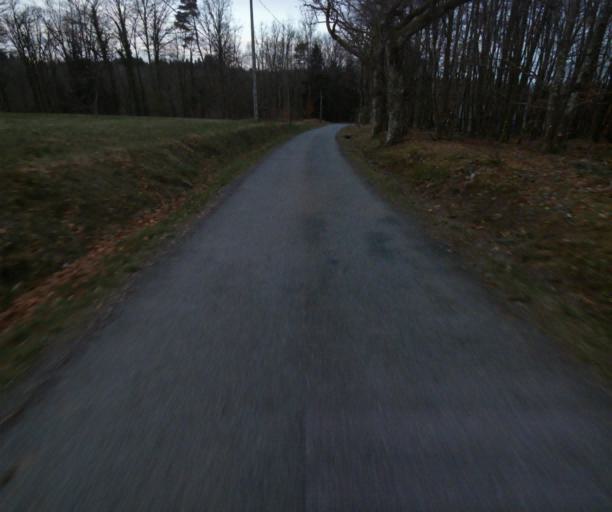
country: FR
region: Limousin
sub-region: Departement de la Correze
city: Correze
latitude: 45.4345
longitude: 1.8423
